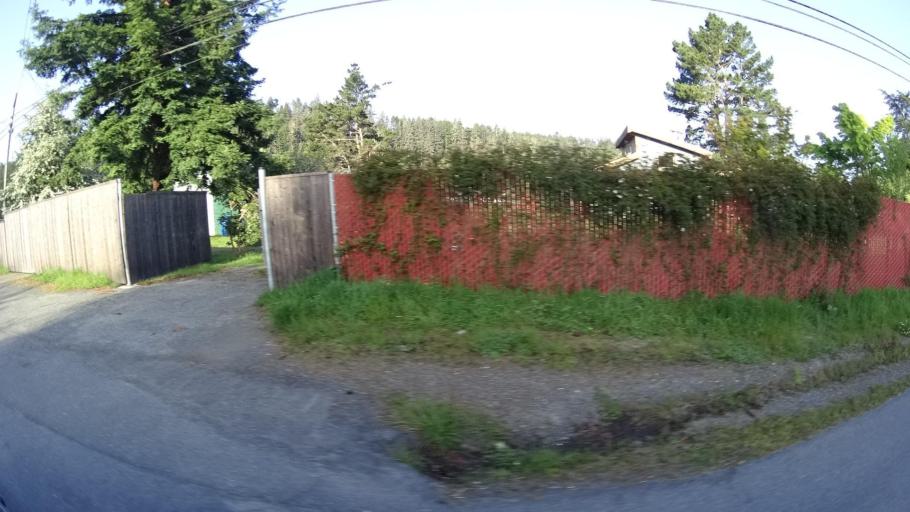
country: US
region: California
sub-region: Humboldt County
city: Myrtletown
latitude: 40.7717
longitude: -124.0737
